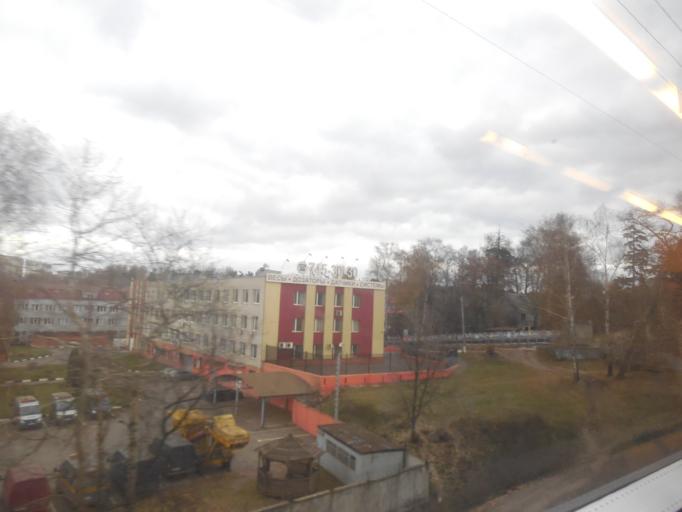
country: RU
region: Moskovskaya
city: Kraskovo
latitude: 55.6507
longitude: 37.9786
